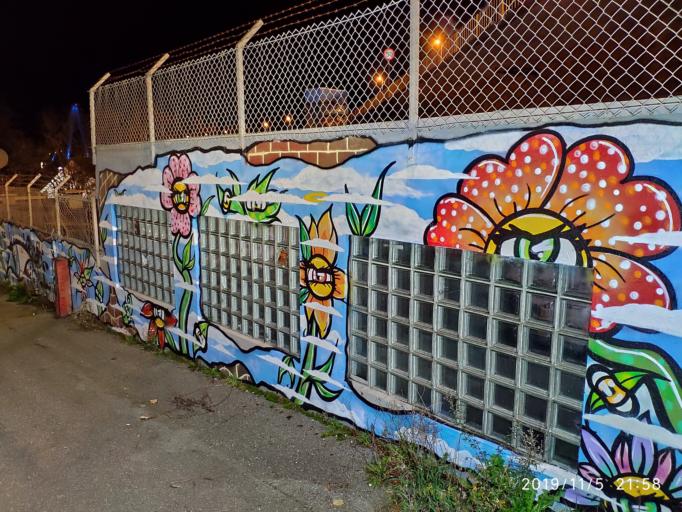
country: NO
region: Rogaland
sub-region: Stavanger
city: Stavanger
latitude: 58.9697
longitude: 5.7480
